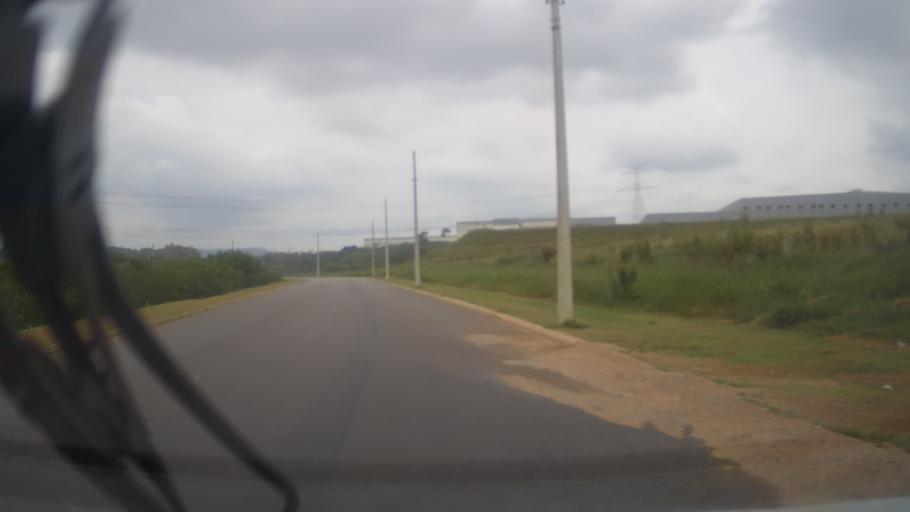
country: BR
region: Sao Paulo
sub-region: Itupeva
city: Itupeva
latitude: -23.1547
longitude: -46.9983
